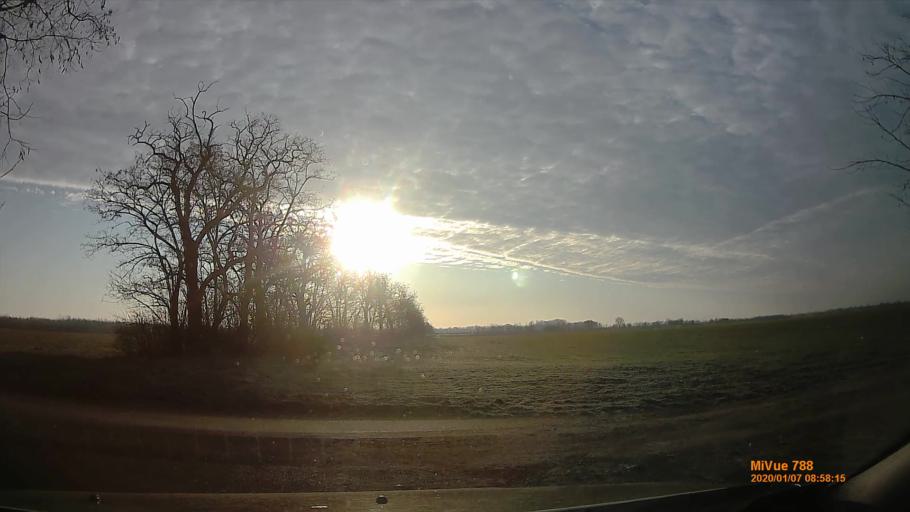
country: HU
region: Gyor-Moson-Sopron
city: Rajka
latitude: 47.9859
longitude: 17.1815
